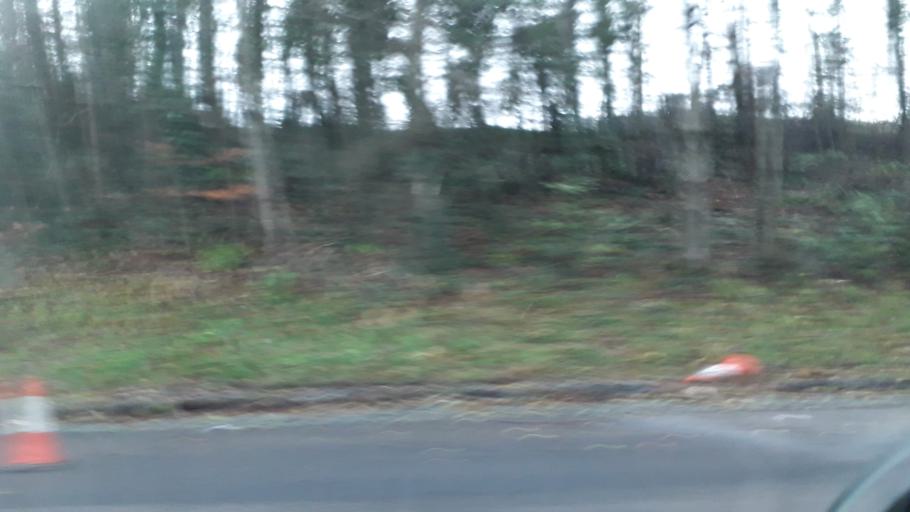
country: IE
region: Ulster
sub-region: County Donegal
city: Raphoe
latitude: 54.9411
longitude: -7.6219
